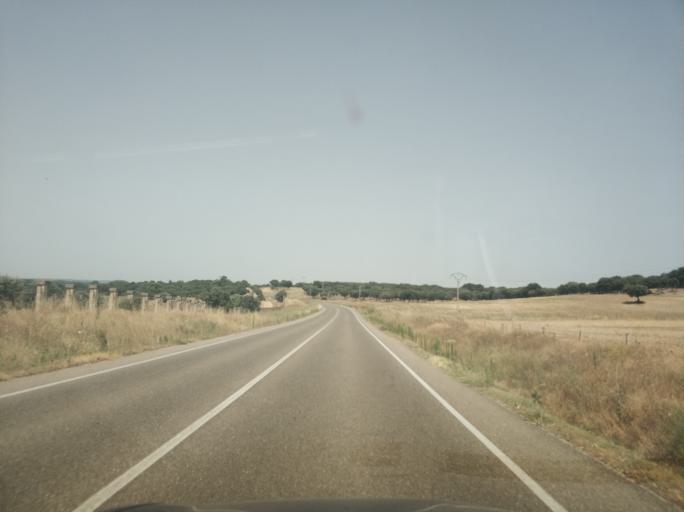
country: ES
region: Castille and Leon
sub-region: Provincia de Salamanca
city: Florida de Liebana
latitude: 41.0365
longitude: -5.7370
